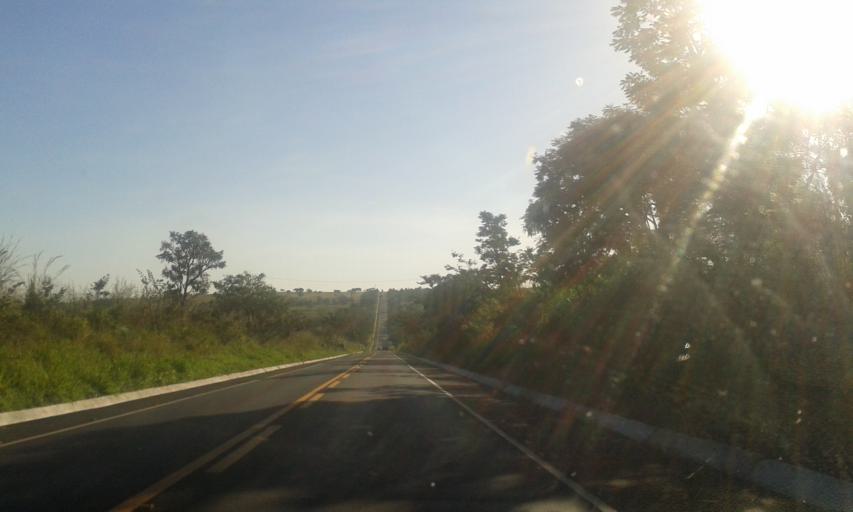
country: BR
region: Minas Gerais
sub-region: Monte Alegre De Minas
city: Monte Alegre de Minas
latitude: -18.8797
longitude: -49.1195
